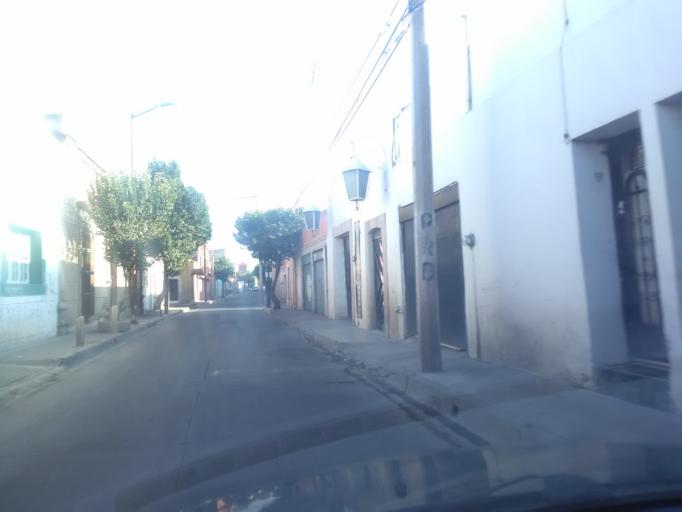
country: MX
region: Durango
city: Victoria de Durango
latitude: 24.0217
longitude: -104.6646
